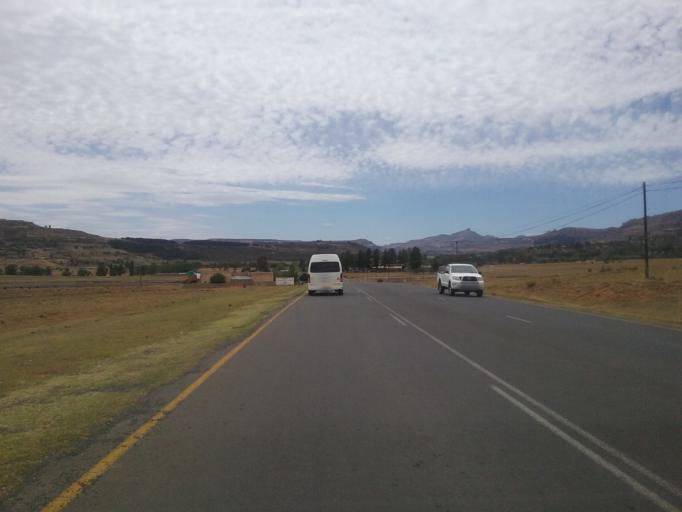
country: LS
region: Maseru
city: Nako
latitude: -29.6255
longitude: 27.4902
